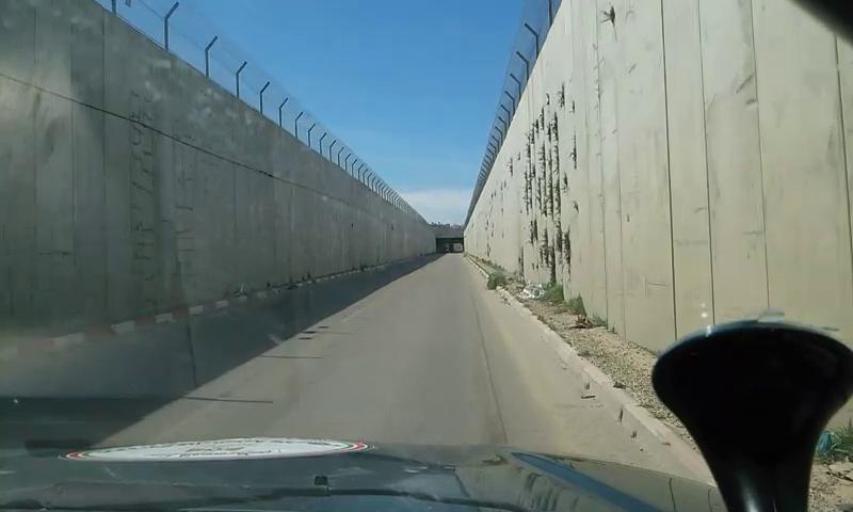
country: IL
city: Giv'on HaHadasha
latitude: 31.8401
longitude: 35.1659
